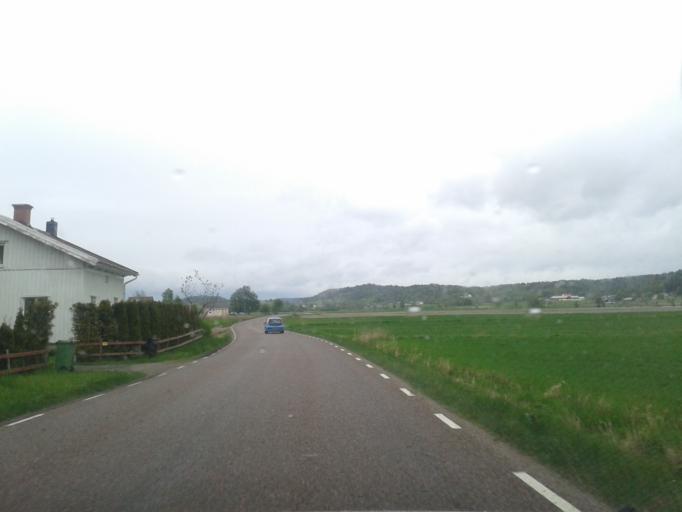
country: SE
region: Vaestra Goetaland
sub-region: Lilla Edets Kommun
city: Lodose
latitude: 58.0425
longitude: 12.1372
